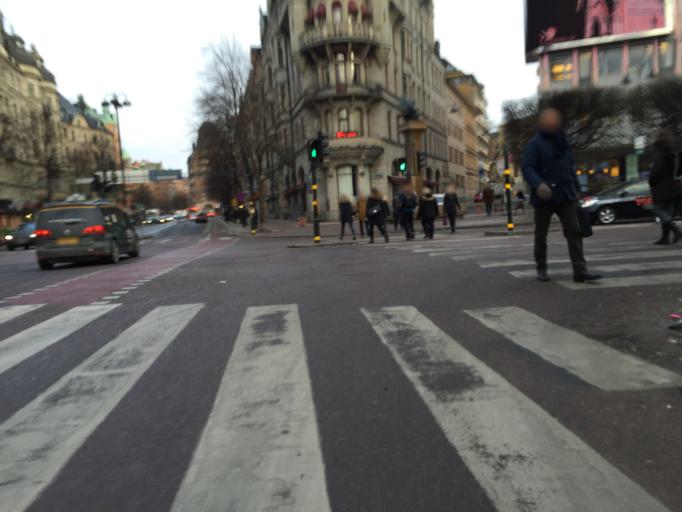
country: SE
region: Stockholm
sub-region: Stockholms Kommun
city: Stockholm
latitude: 59.3361
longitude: 18.0726
